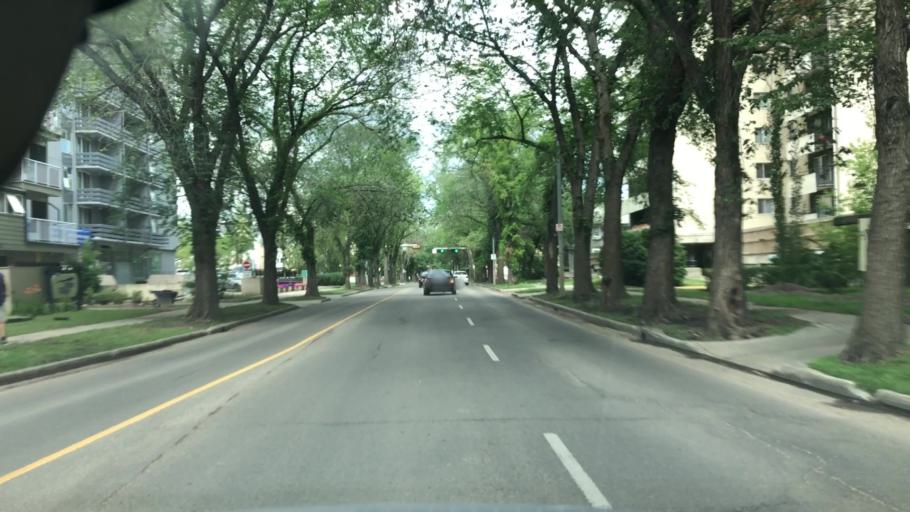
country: CA
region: Alberta
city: Edmonton
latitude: 53.5416
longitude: -113.5213
